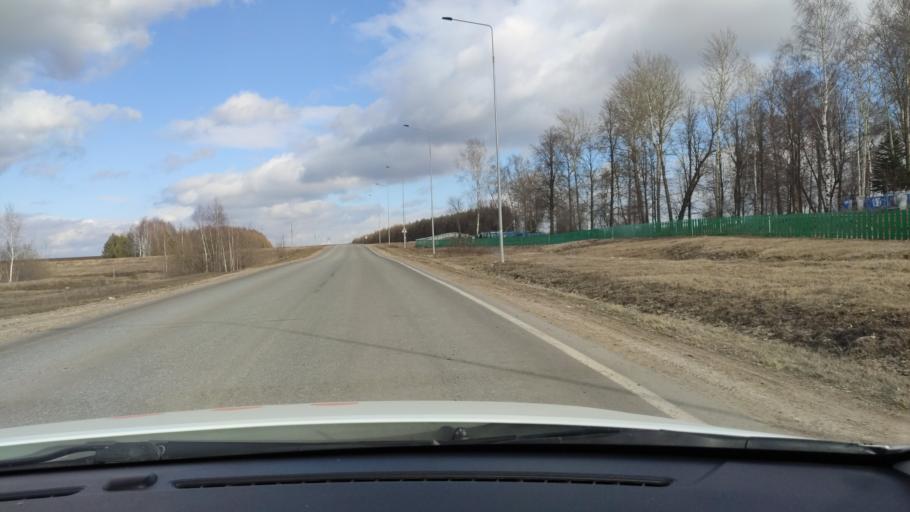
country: RU
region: Tatarstan
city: Vysokaya Gora
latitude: 56.2226
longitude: 49.2814
